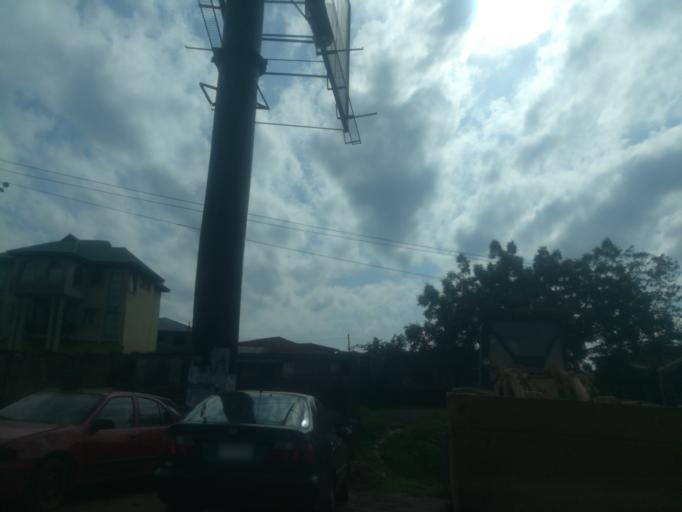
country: NG
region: Oyo
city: Ibadan
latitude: 7.3940
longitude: 3.9382
